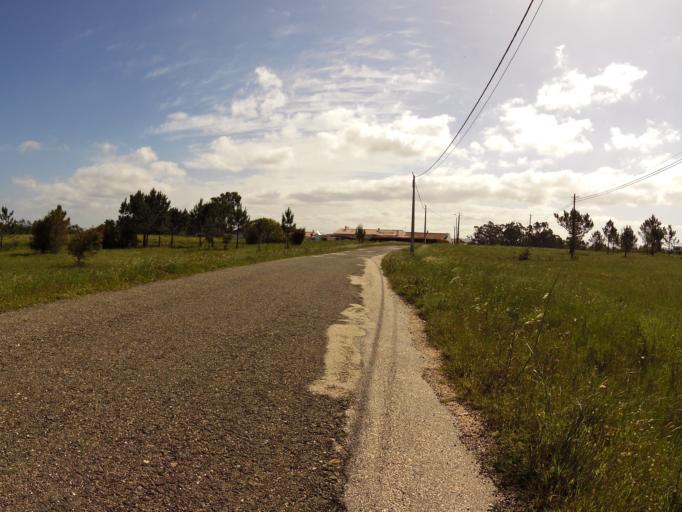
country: PT
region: Faro
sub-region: Aljezur
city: Aljezur
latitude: 37.3407
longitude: -8.8035
